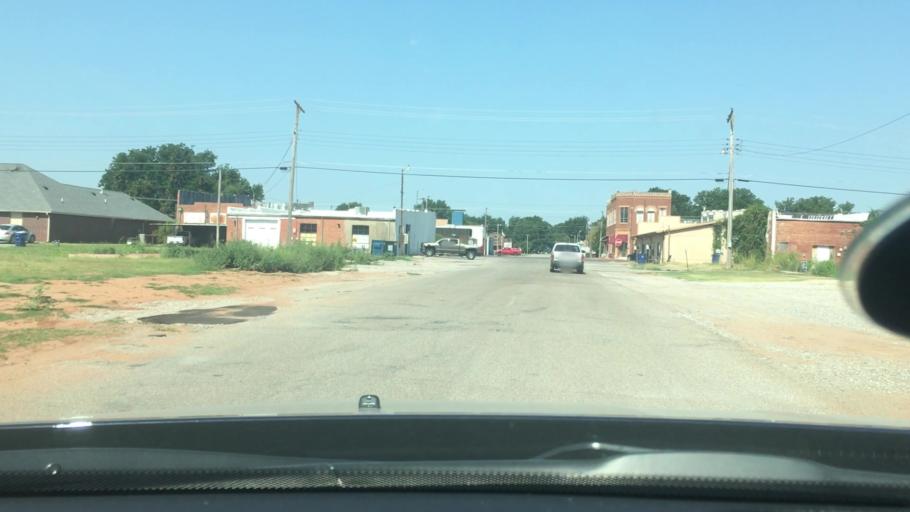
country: US
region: Oklahoma
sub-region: Garvin County
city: Lindsay
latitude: 34.8336
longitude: -97.6014
